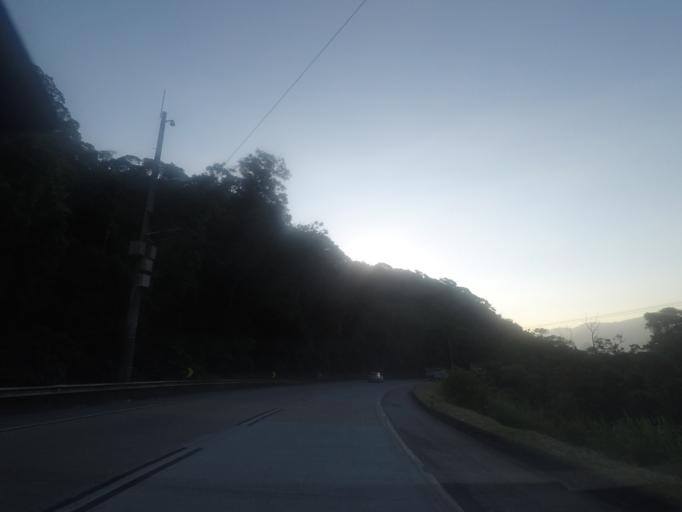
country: BR
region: Rio de Janeiro
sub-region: Petropolis
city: Petropolis
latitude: -22.5221
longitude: -43.2318
